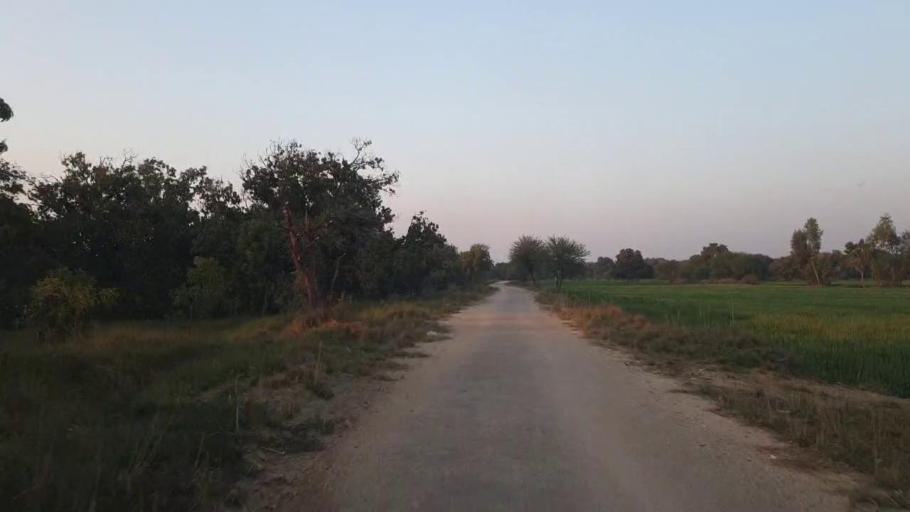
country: PK
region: Sindh
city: Chambar
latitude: 25.4151
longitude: 68.8659
